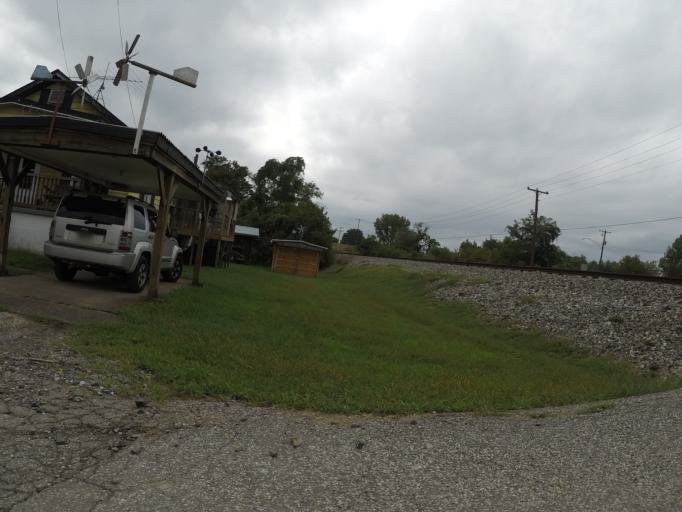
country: US
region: West Virginia
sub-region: Cabell County
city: Pea Ridge
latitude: 38.4306
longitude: -82.3721
